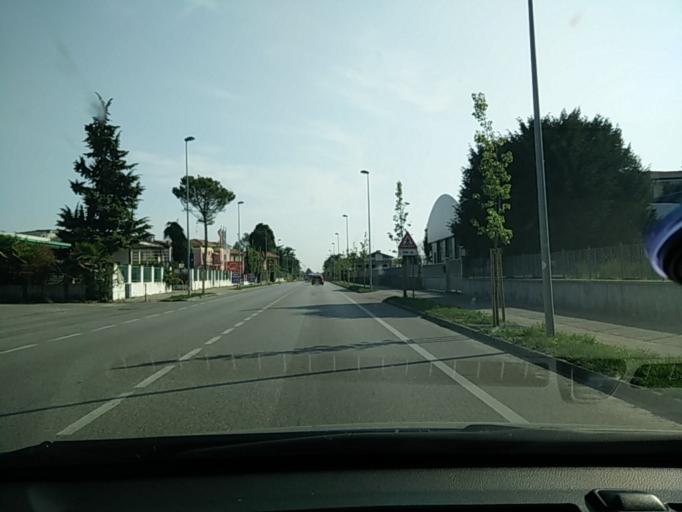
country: IT
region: Friuli Venezia Giulia
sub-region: Provincia di Pordenone
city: Prata di Sotto
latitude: 45.8938
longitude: 12.5939
